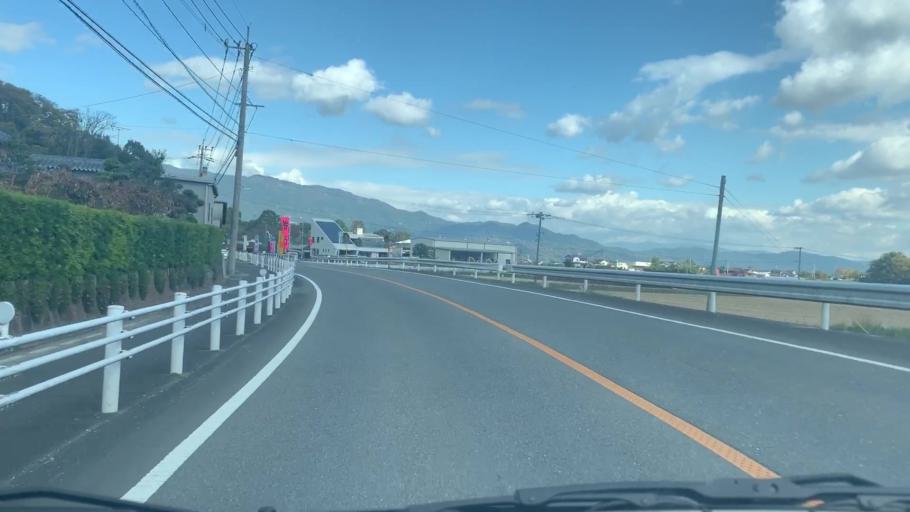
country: JP
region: Saga Prefecture
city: Saga-shi
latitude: 33.2684
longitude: 130.1803
